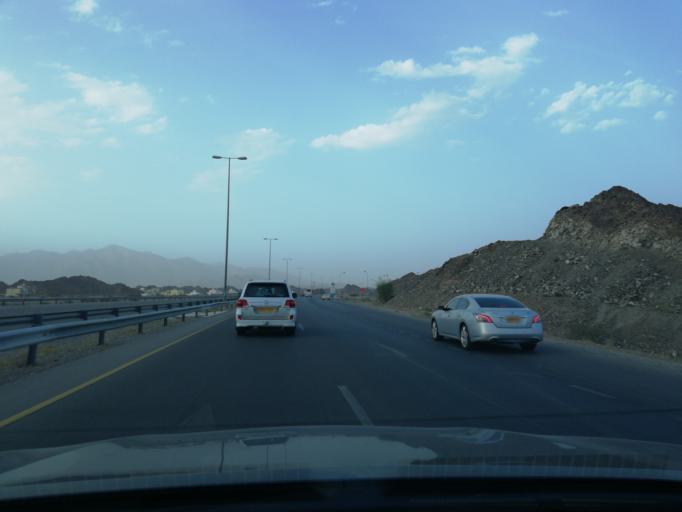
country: OM
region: Muhafazat ad Dakhiliyah
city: Sufalat Sama'il
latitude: 23.3201
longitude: 57.9596
